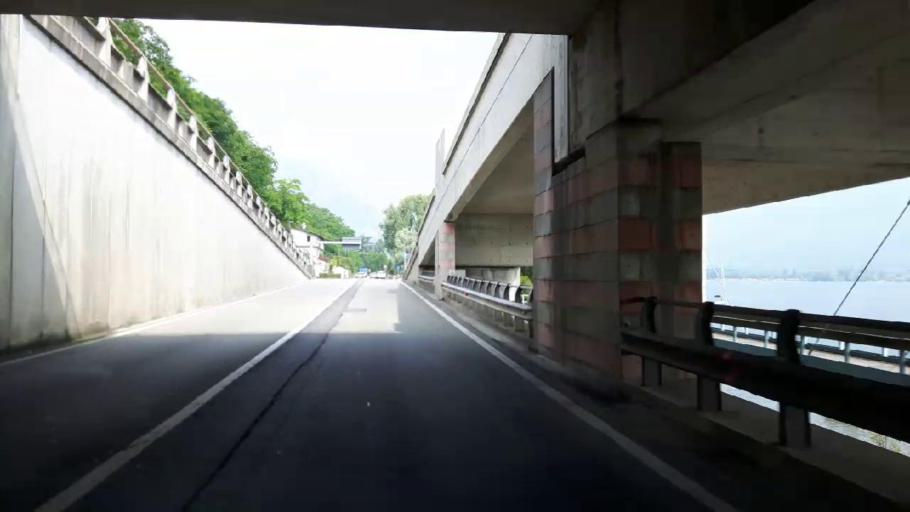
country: IT
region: Piedmont
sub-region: Provincia Verbano-Cusio-Ossola
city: Baveno
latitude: 45.9214
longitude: 8.4927
